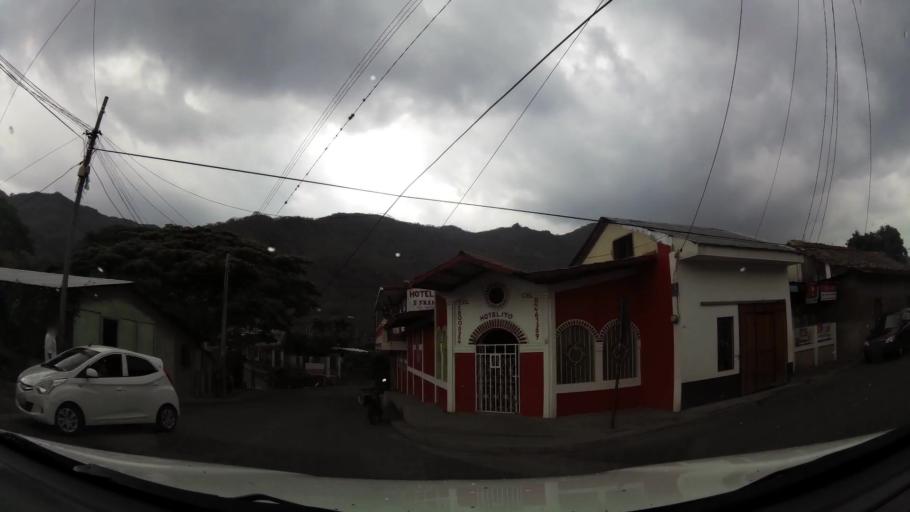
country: NI
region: Jinotega
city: Jinotega
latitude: 13.0890
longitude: -86.0037
